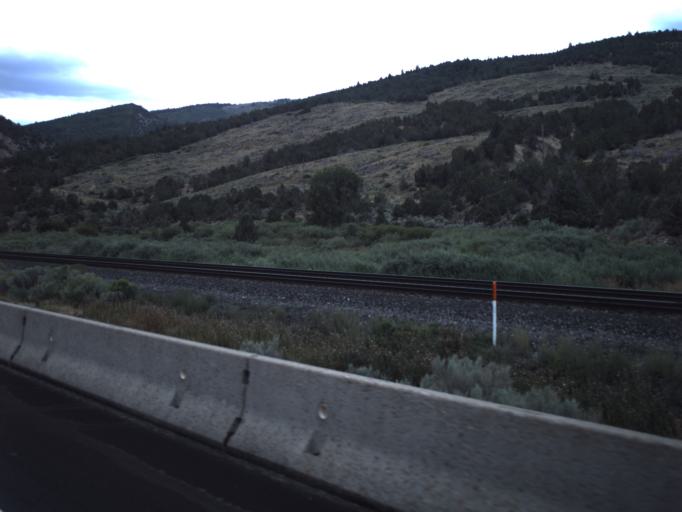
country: US
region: Utah
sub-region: Utah County
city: Mapleton
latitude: 39.9540
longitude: -111.2948
